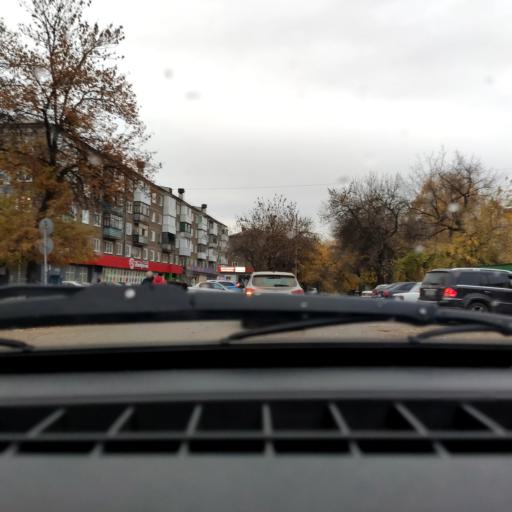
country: RU
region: Bashkortostan
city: Ufa
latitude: 54.8038
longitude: 56.1258
